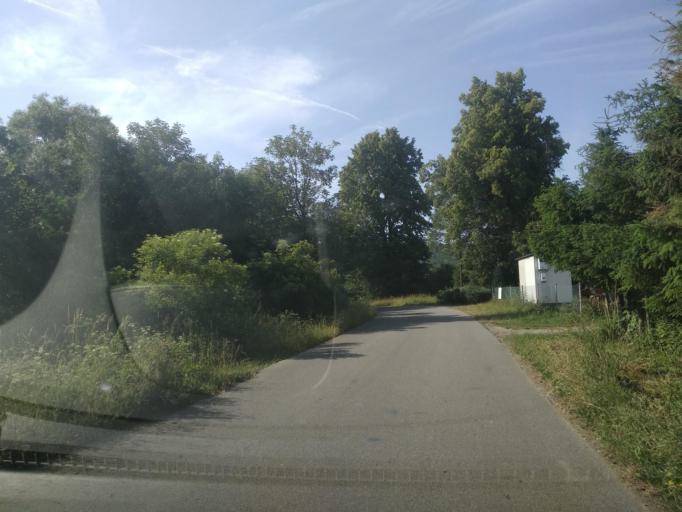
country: PL
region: Subcarpathian Voivodeship
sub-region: Powiat krosnienski
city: Jasliska
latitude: 49.4251
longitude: 21.8535
